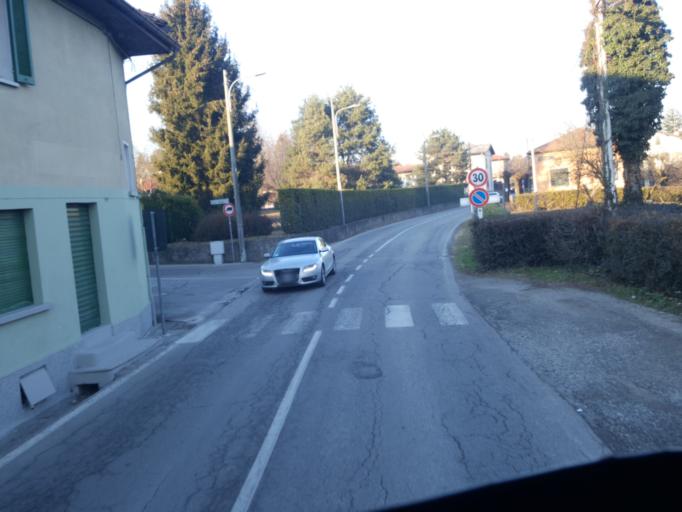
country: IT
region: Piedmont
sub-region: Provincia di Novara
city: Varallo Pombia
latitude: 45.6869
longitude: 8.6311
